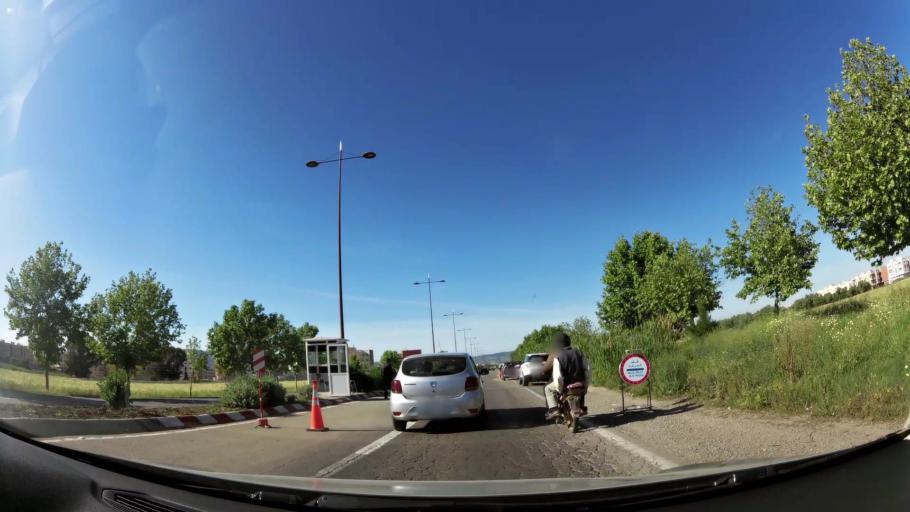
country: MA
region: Fes-Boulemane
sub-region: Fes
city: Fes
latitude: 34.0076
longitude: -5.0216
